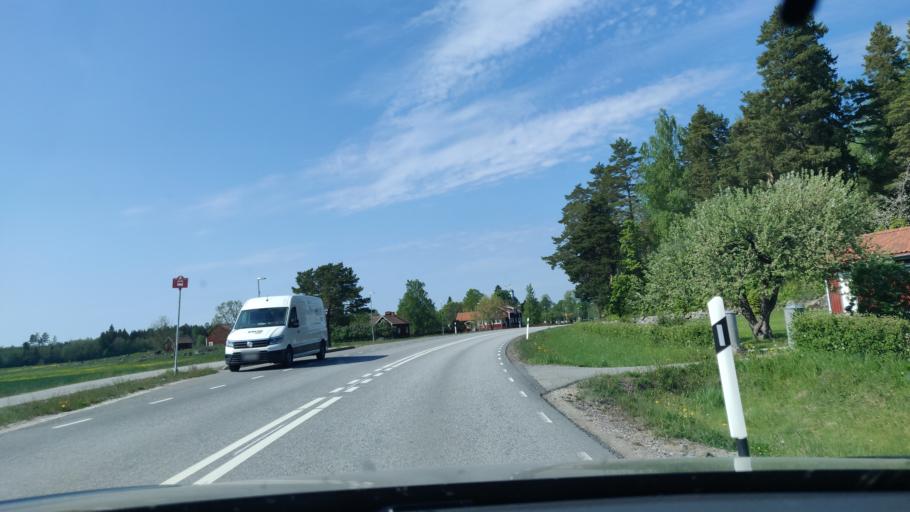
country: SE
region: Uppsala
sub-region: Heby Kommun
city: OEstervala
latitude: 60.1732
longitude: 17.1818
